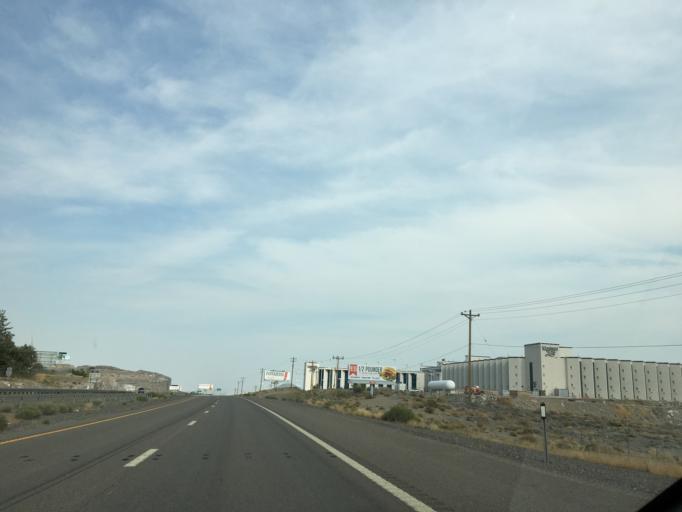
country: US
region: Utah
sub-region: Tooele County
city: Wendover
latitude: 40.7378
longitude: -114.0490
